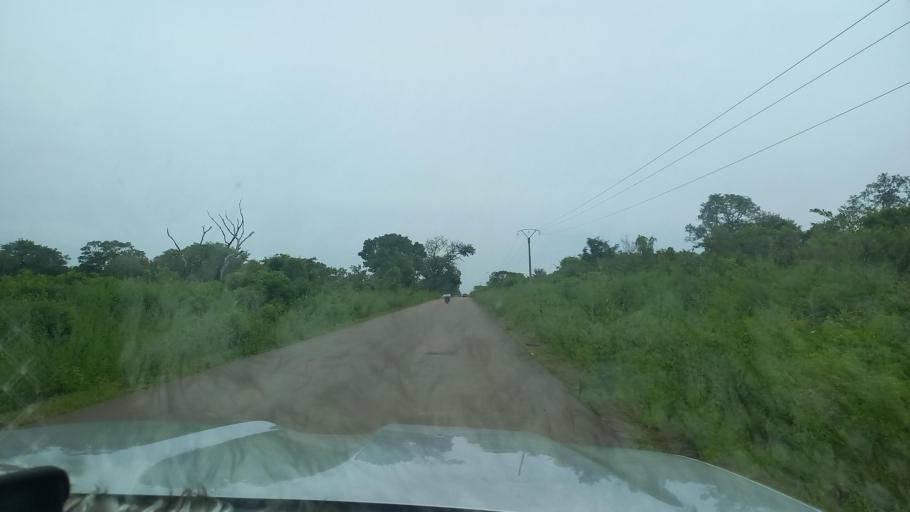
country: SN
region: Ziguinchor
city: Bignona
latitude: 12.8290
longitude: -16.1674
